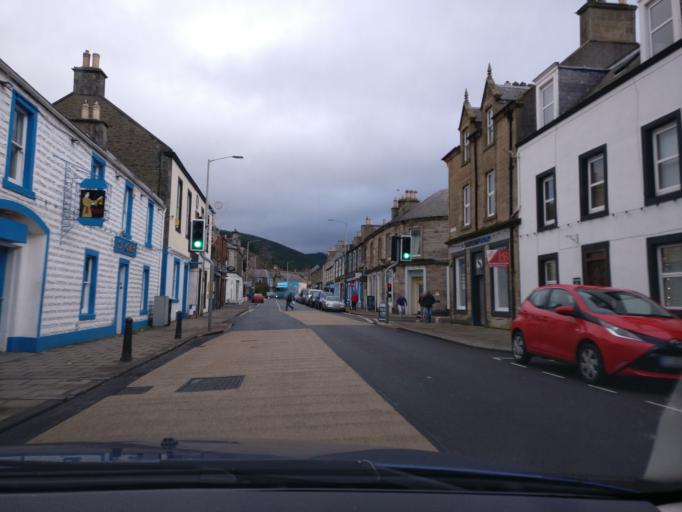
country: GB
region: Scotland
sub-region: The Scottish Borders
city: Innerleithen
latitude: 55.6192
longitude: -3.0634
